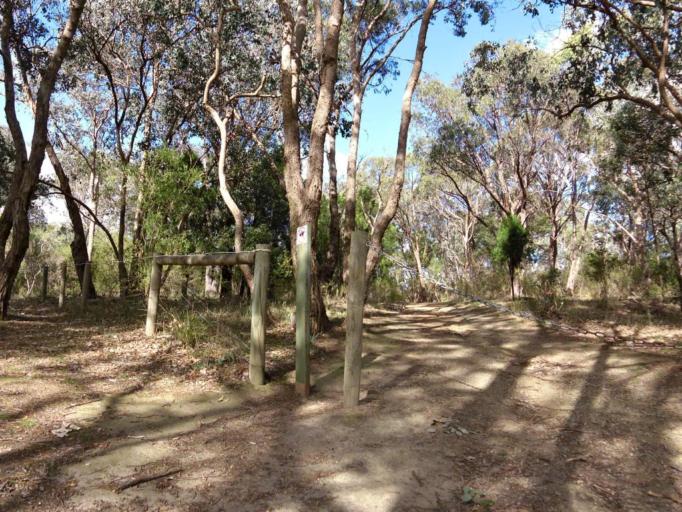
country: AU
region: Victoria
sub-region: Manningham
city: Park Orchards
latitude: -37.7734
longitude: 145.2274
